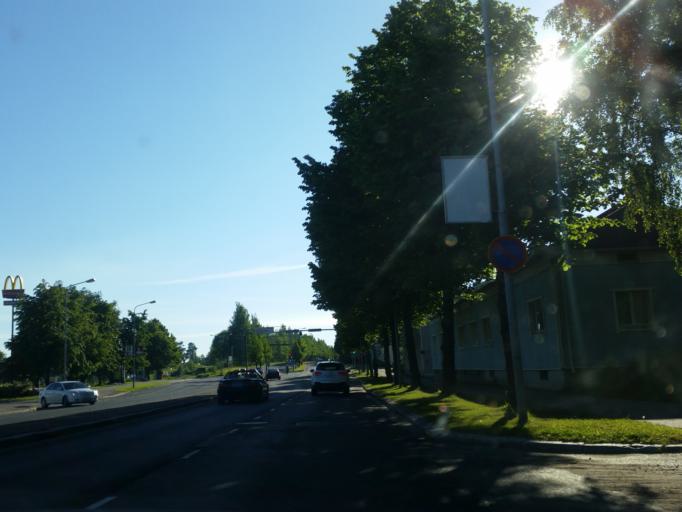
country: FI
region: Northern Savo
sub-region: Kuopio
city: Kuopio
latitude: 62.8822
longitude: 27.6666
